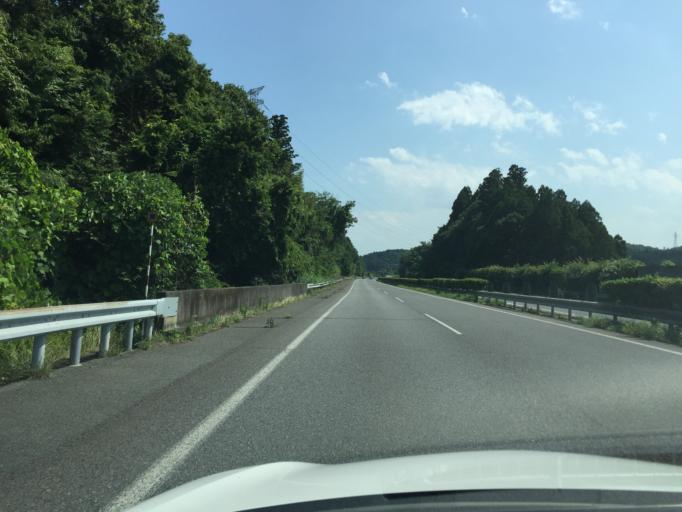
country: JP
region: Fukushima
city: Iwaki
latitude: 36.9423
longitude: 140.7721
